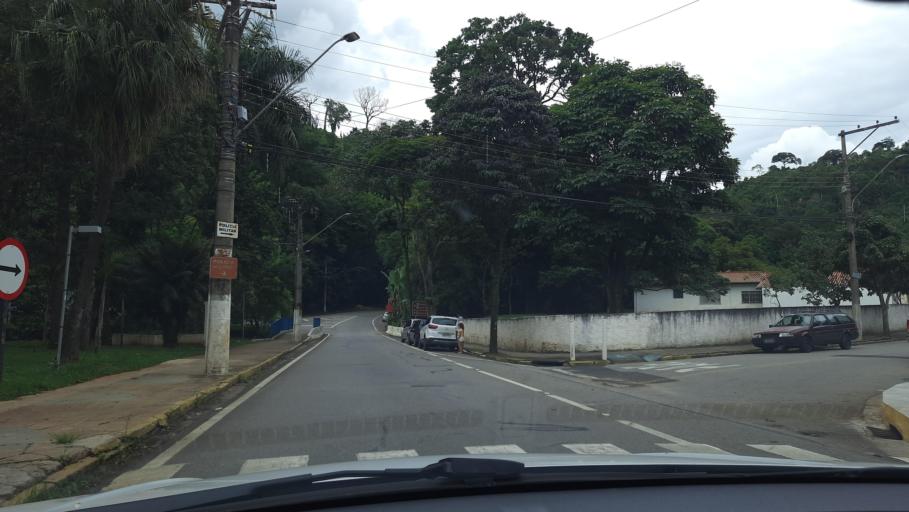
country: BR
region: Sao Paulo
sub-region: Sao Joao Da Boa Vista
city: Sao Joao da Boa Vista
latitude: -21.9344
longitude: -46.7152
